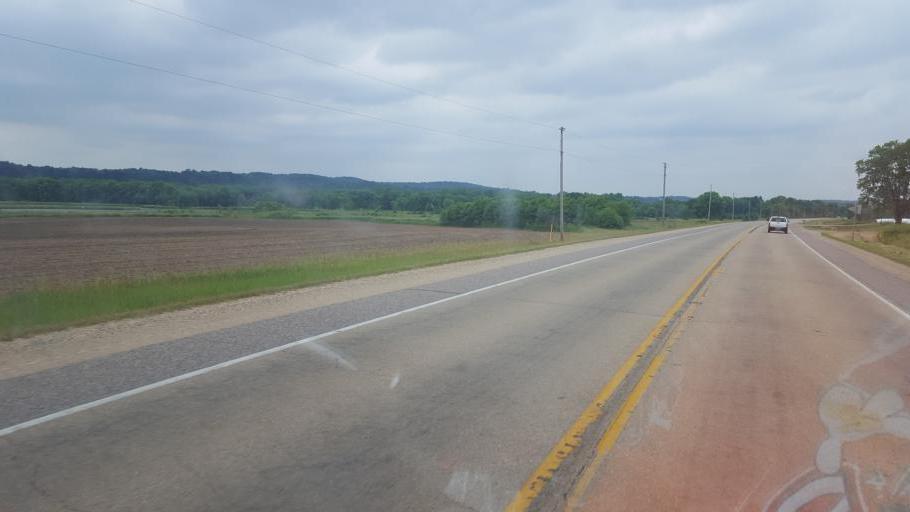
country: US
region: Wisconsin
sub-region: Juneau County
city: Elroy
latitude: 43.6209
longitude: -90.1582
